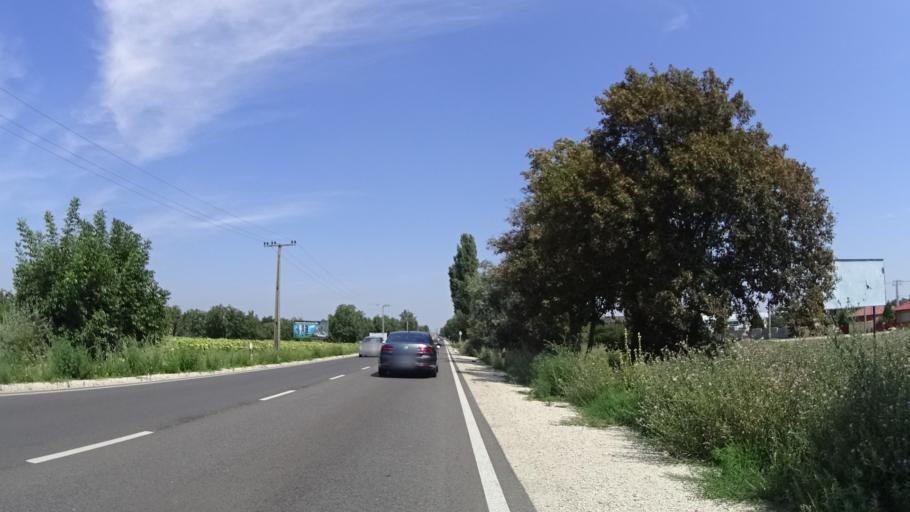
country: HU
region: Fejer
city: Szekesfehervar
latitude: 47.1540
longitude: 18.3988
